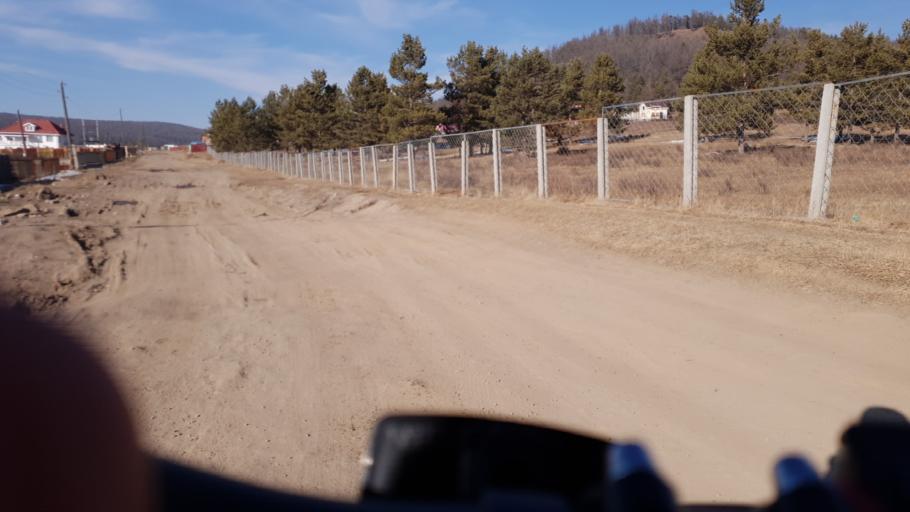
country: MN
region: Ulaanbaatar
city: Ulaanbaatar
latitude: 48.1498
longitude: 106.8871
